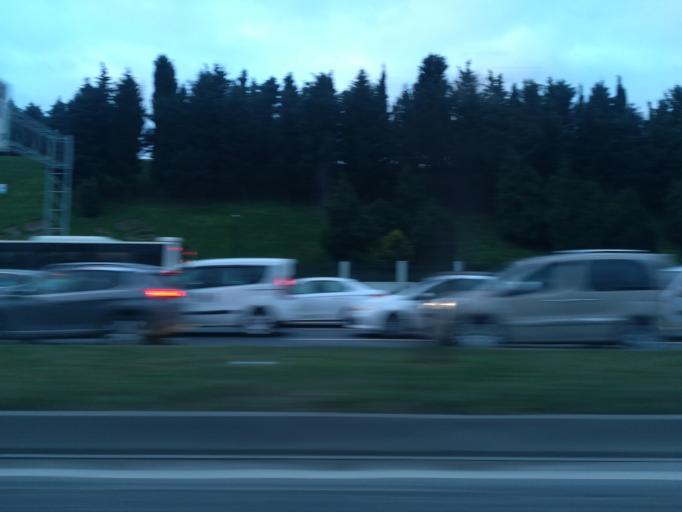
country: TR
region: Istanbul
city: Istanbul
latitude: 41.0263
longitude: 28.9269
